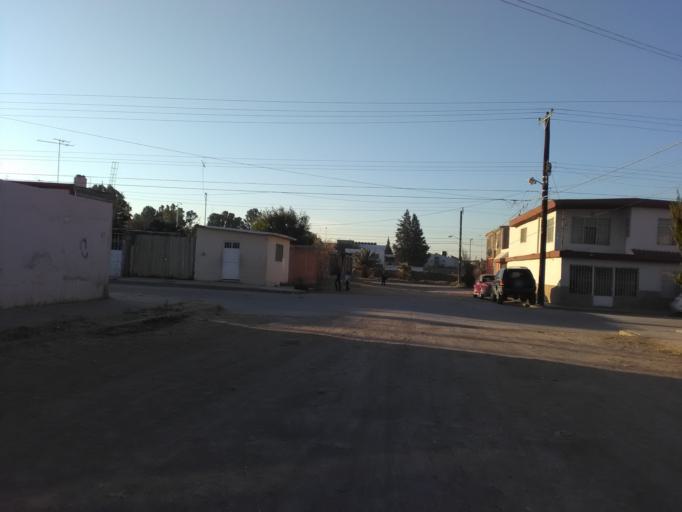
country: MX
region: Durango
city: Victoria de Durango
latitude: 24.0511
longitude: -104.6380
